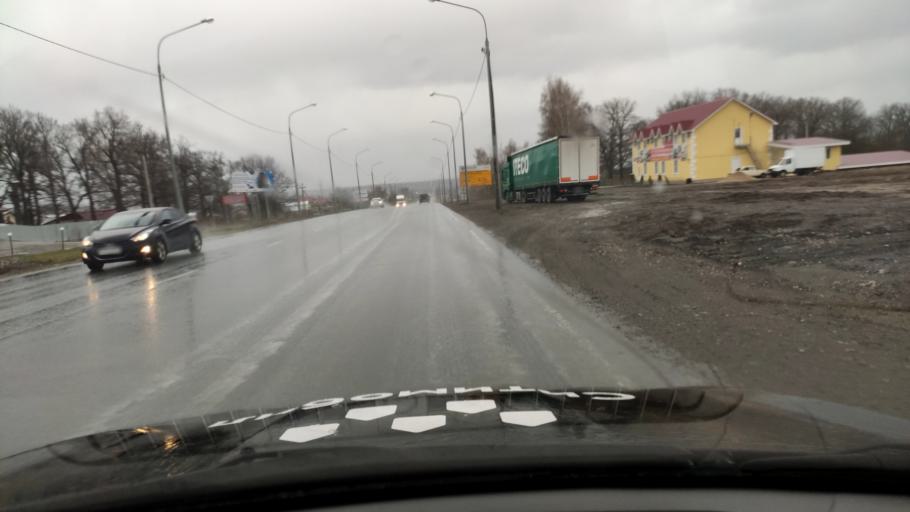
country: RU
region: Samara
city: Zhigulevsk
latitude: 53.3787
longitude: 49.4561
